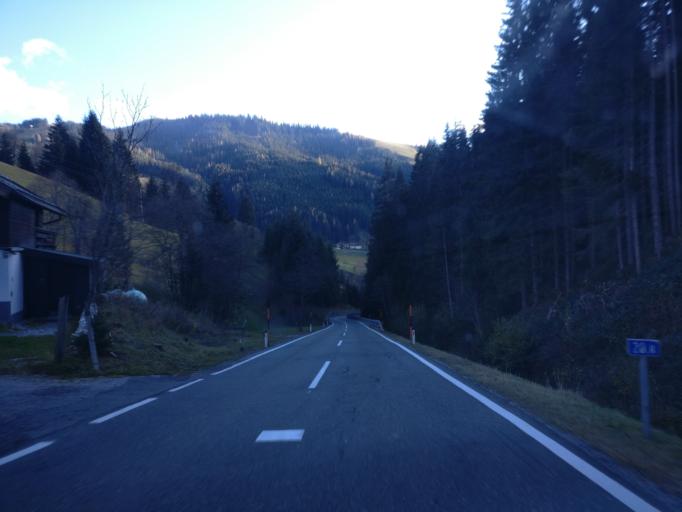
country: AT
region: Salzburg
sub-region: Politischer Bezirk Zell am See
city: Dienten am Hochkonig
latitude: 47.3934
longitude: 13.0151
